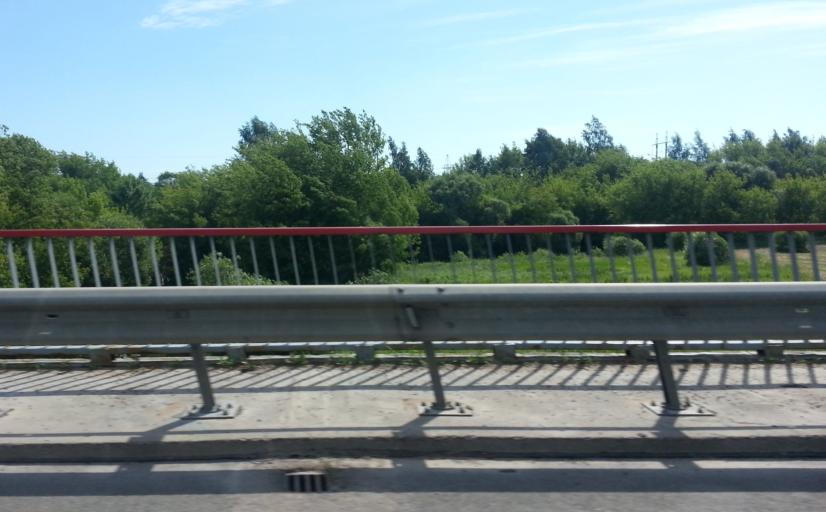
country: LT
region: Panevezys
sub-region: Panevezys City
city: Panevezys
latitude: 55.7397
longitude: 24.2768
